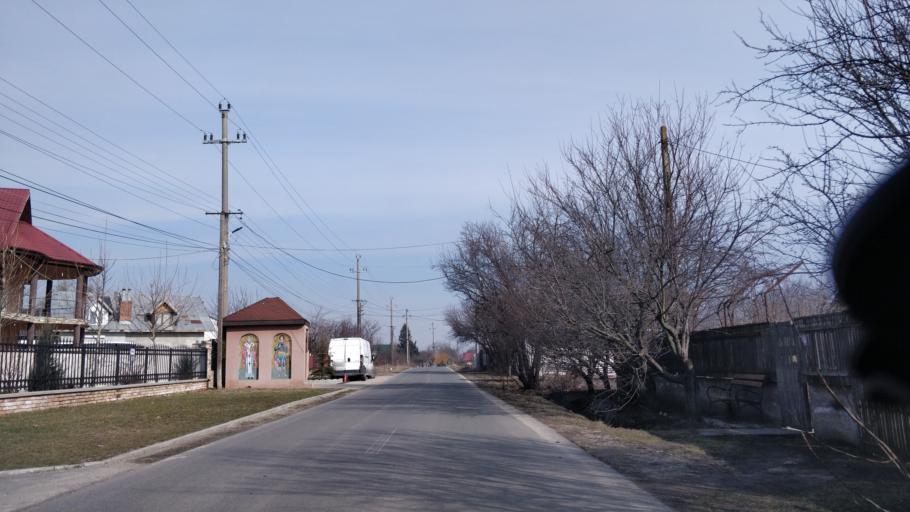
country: RO
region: Giurgiu
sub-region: Comuna Ulmi
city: Ulmi
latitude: 44.4767
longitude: 25.7671
